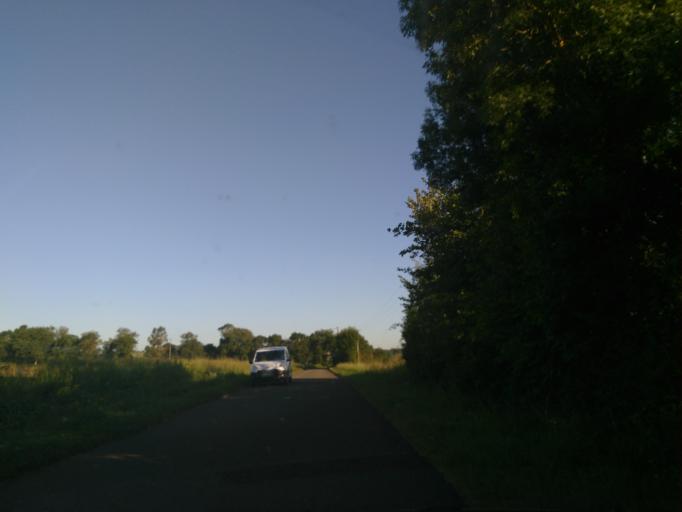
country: FR
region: Midi-Pyrenees
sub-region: Departement du Gers
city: Valence-sur-Baise
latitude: 43.8745
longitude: 0.4294
